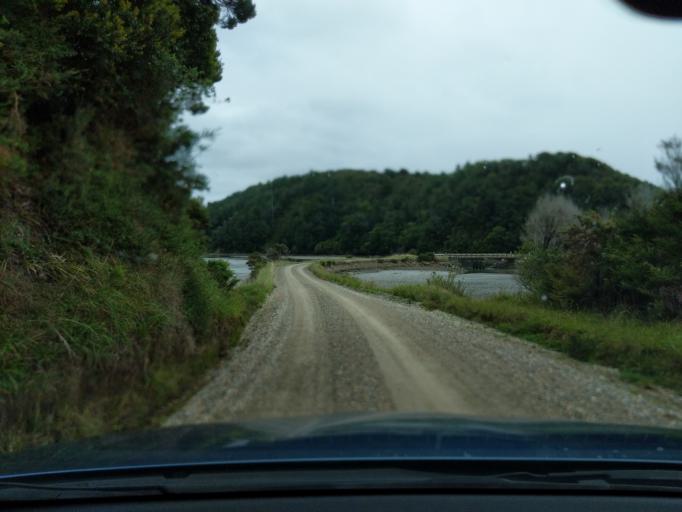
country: NZ
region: Tasman
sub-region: Tasman District
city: Takaka
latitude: -40.6275
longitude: 172.5158
